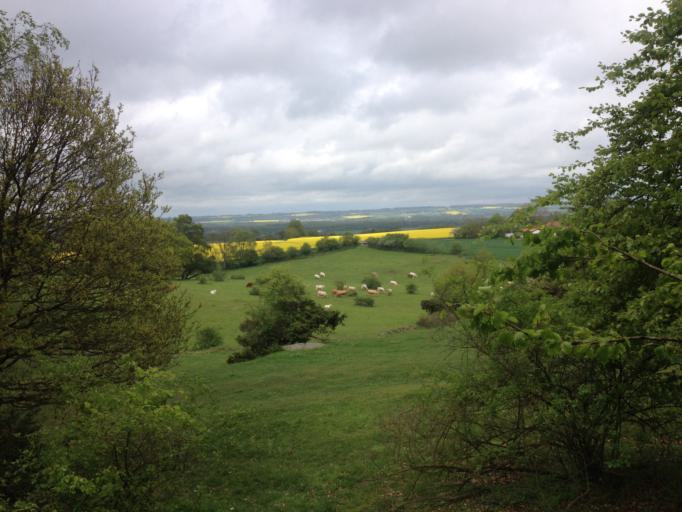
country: SE
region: Skane
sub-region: Lunds Kommun
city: Genarp
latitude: 55.6991
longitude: 13.3689
